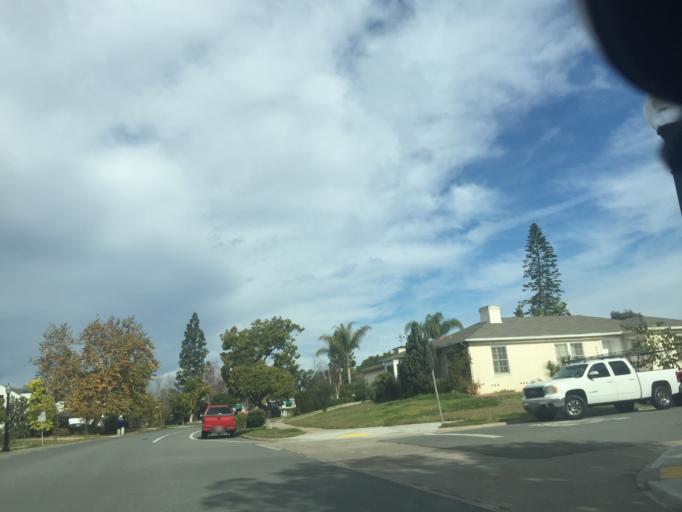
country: US
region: California
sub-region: San Diego County
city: Lemon Grove
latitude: 32.7608
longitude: -117.0917
